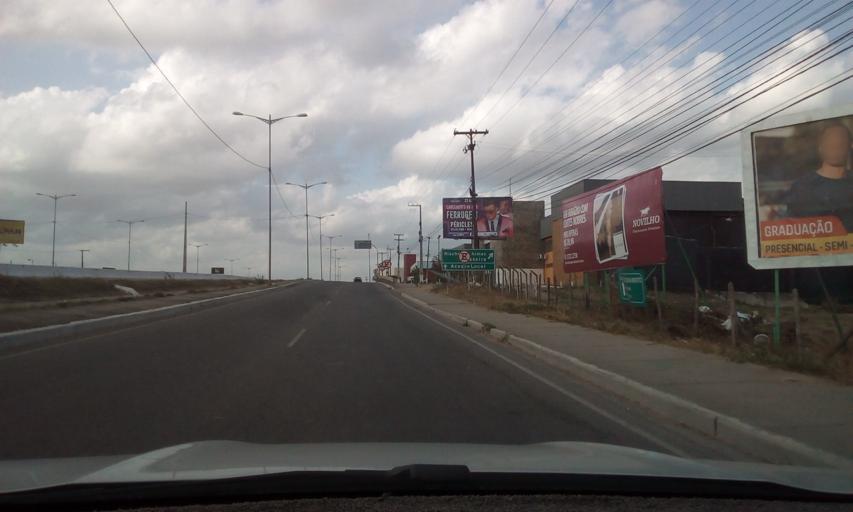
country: BR
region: Pernambuco
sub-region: Caruaru
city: Caruaru
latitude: -8.2540
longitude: -35.9751
